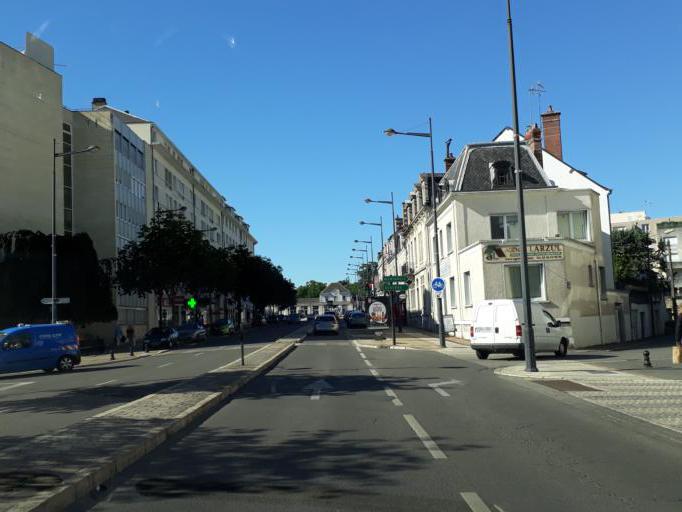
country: FR
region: Centre
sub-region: Departement du Cher
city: Bourges
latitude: 47.0919
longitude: 2.3938
